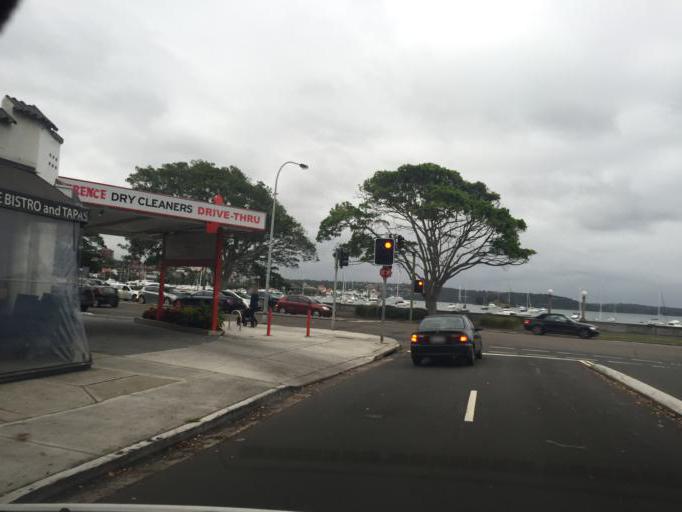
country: AU
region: New South Wales
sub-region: Woollahra
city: Bellevue Hill
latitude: -33.8728
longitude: 151.2598
